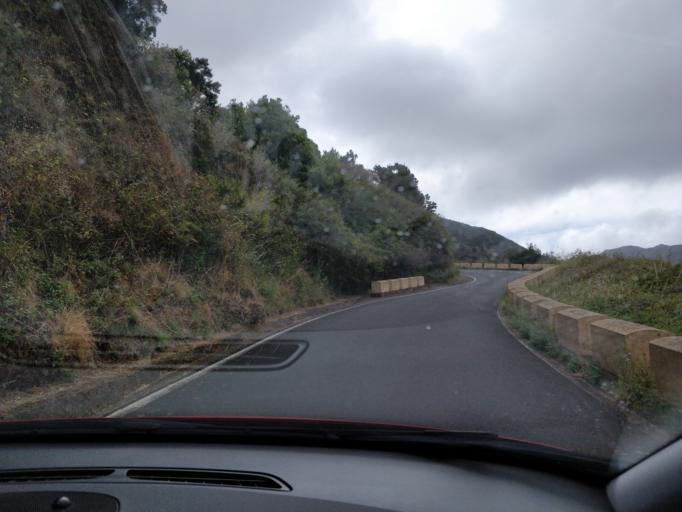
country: ES
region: Canary Islands
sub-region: Provincia de Santa Cruz de Tenerife
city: Santiago del Teide
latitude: 28.3222
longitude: -16.8452
